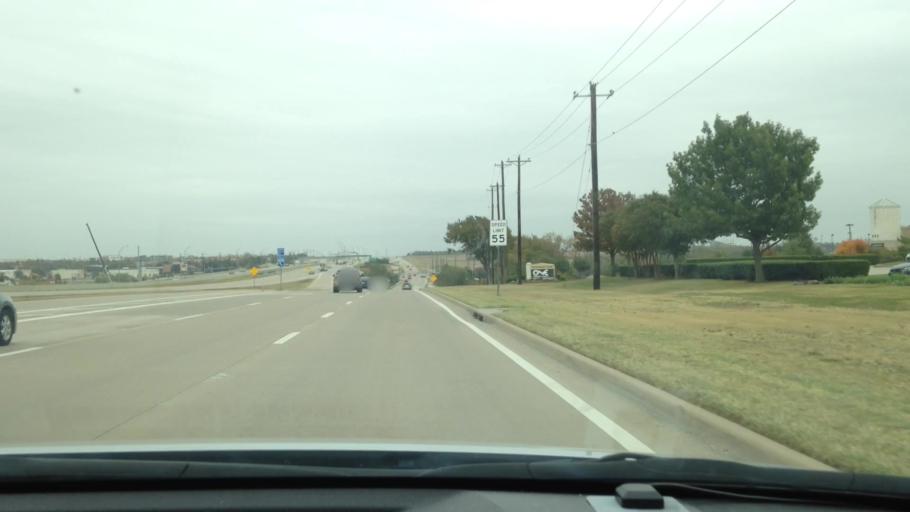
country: US
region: Texas
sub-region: Collin County
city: Allen
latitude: 33.1223
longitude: -96.7397
